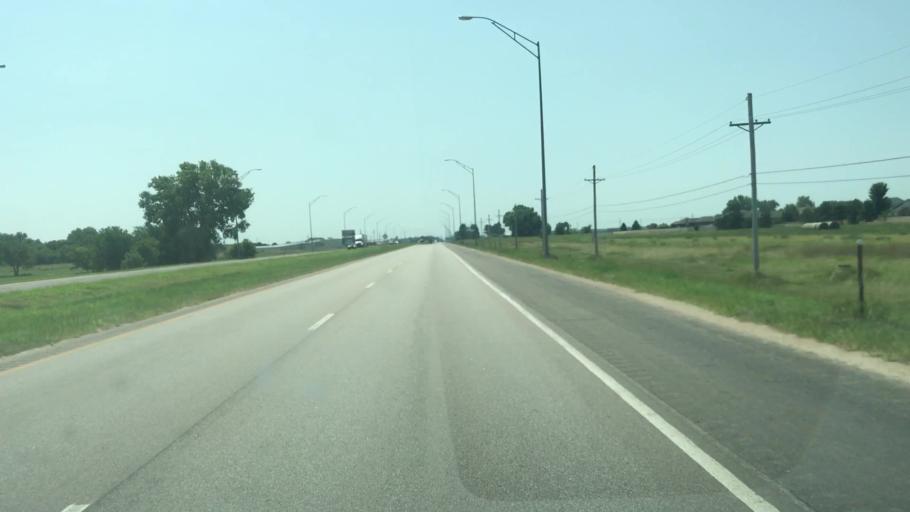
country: US
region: Nebraska
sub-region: Hall County
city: Grand Island
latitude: 40.8787
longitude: -98.3783
